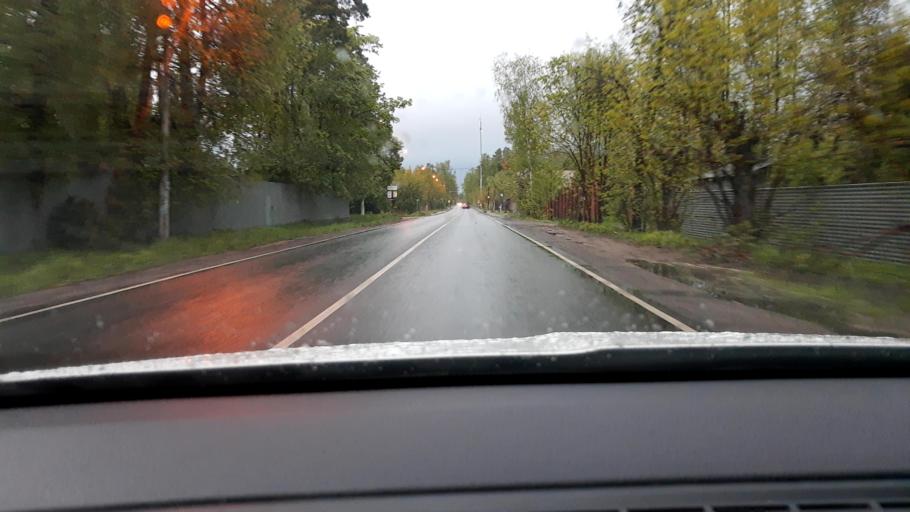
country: RU
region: Moskovskaya
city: Zagoryanskiy
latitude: 55.9166
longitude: 37.9158
